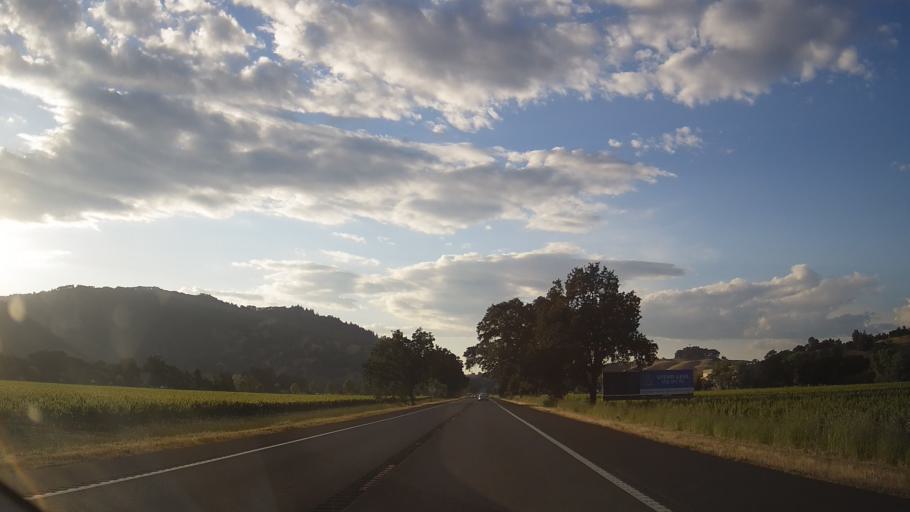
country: US
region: California
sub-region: Mendocino County
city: Talmage
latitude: 39.0402
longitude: -123.1475
